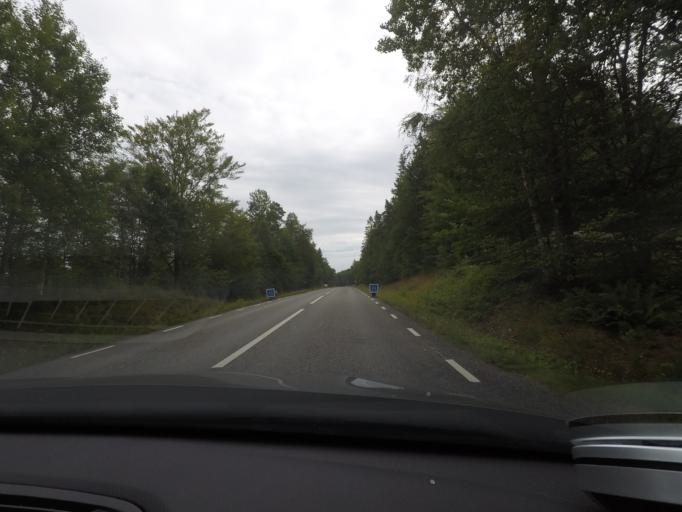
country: SE
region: Blekinge
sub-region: Olofstroms Kommun
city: Olofstroem
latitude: 56.4447
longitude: 14.5121
